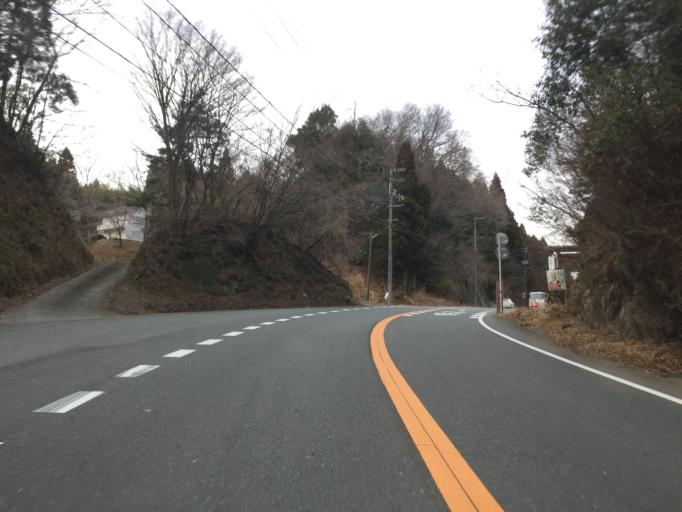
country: JP
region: Fukushima
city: Iwaki
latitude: 36.9718
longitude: 140.7403
